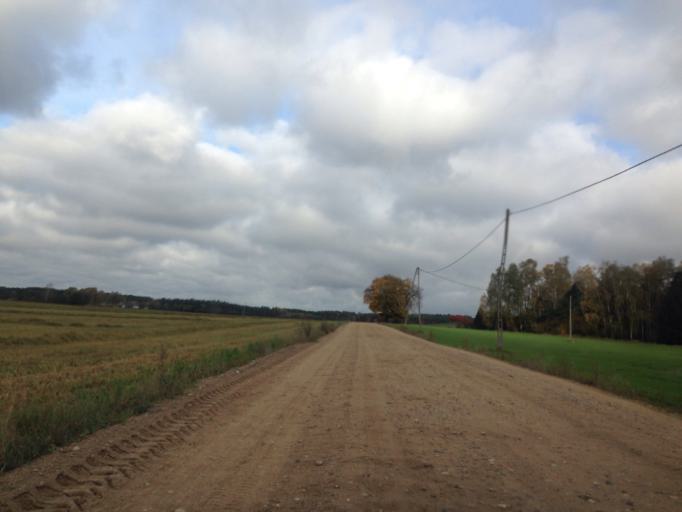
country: PL
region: Kujawsko-Pomorskie
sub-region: Powiat brodnicki
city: Brzozie
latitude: 53.2948
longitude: 19.5733
